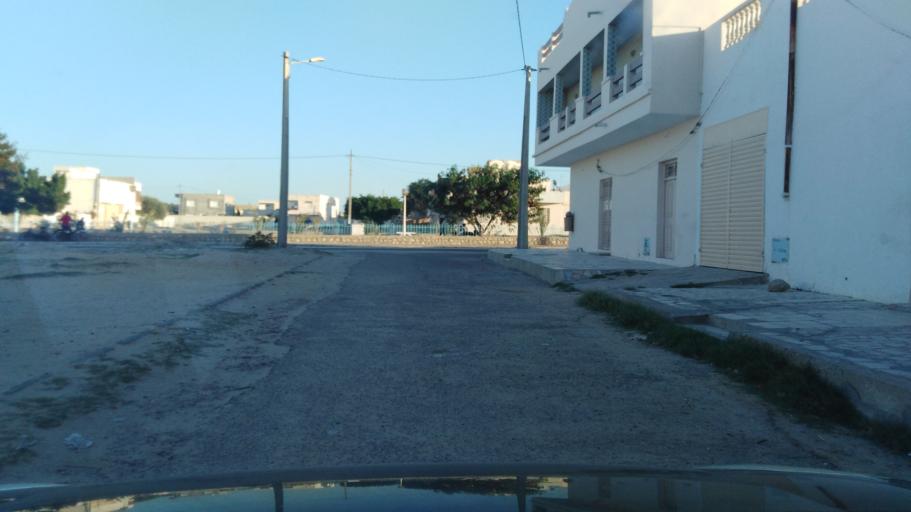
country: TN
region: Qabis
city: Gabes
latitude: 33.9540
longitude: 10.0128
